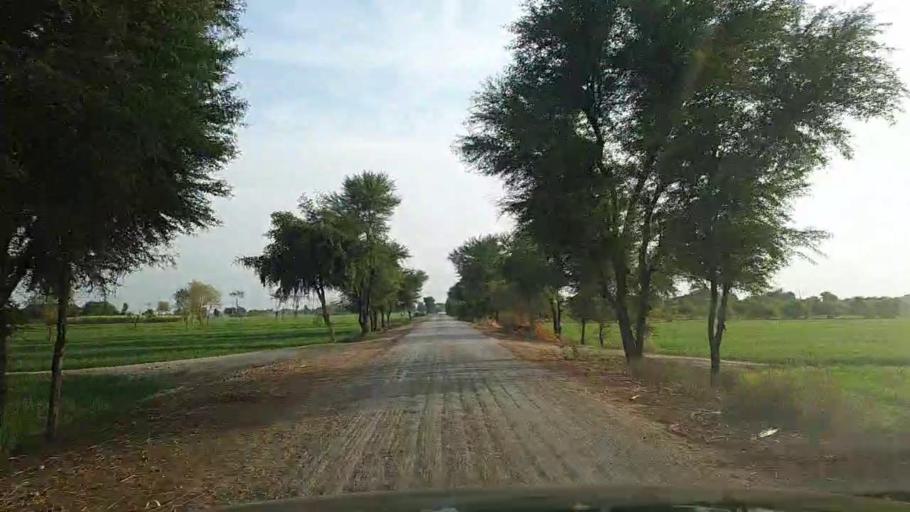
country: PK
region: Sindh
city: Jam Sahib
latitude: 26.4360
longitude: 68.5715
